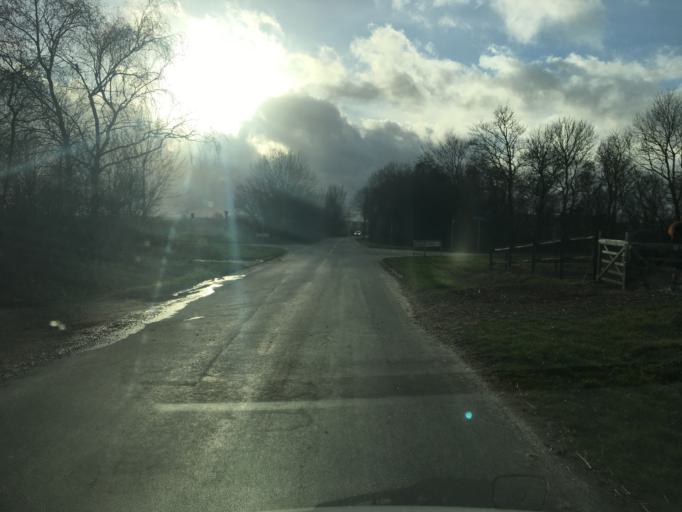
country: DK
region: South Denmark
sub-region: Sonderborg Kommune
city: Grasten
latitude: 54.9631
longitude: 9.5502
